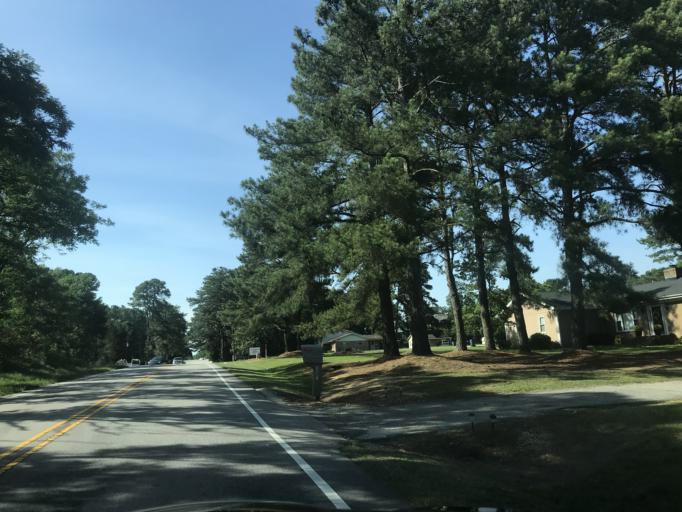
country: US
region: North Carolina
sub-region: Wake County
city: Garner
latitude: 35.6833
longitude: -78.5797
